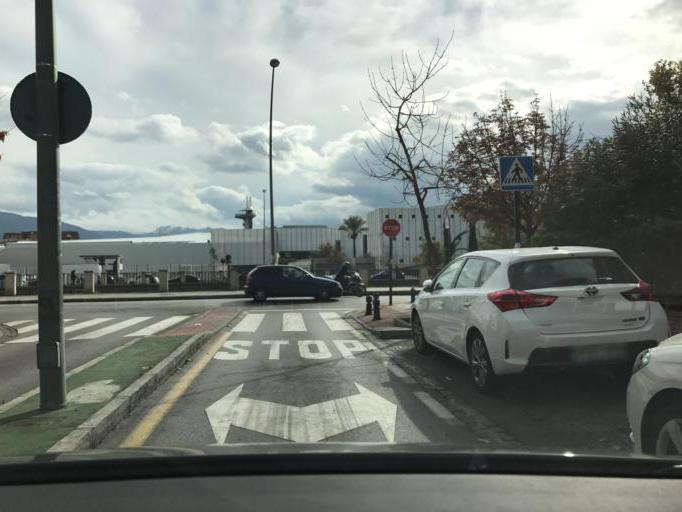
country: ES
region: Andalusia
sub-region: Provincia de Granada
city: Granada
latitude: 37.1645
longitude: -3.6068
